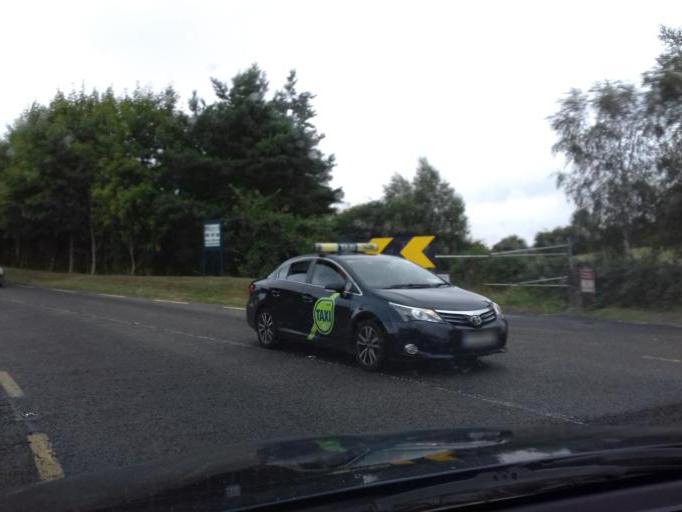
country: IE
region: Leinster
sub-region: County Carlow
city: Bagenalstown
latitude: 52.7443
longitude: -6.9696
